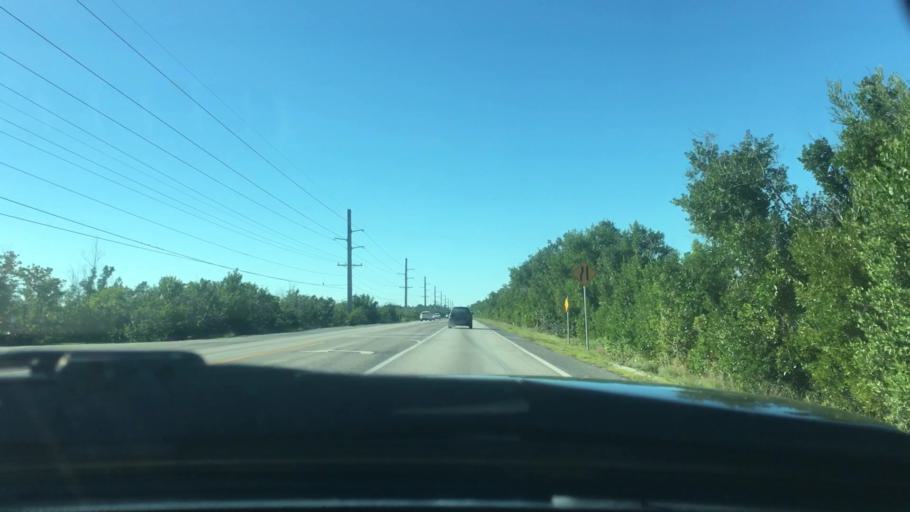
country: US
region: Florida
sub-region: Monroe County
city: Cudjoe Key
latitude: 24.6645
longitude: -81.4865
